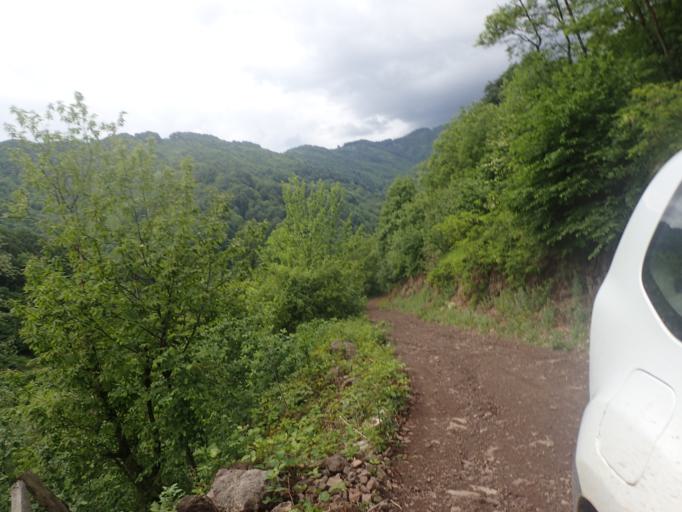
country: TR
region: Samsun
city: Salipazari
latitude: 40.9353
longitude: 36.8550
